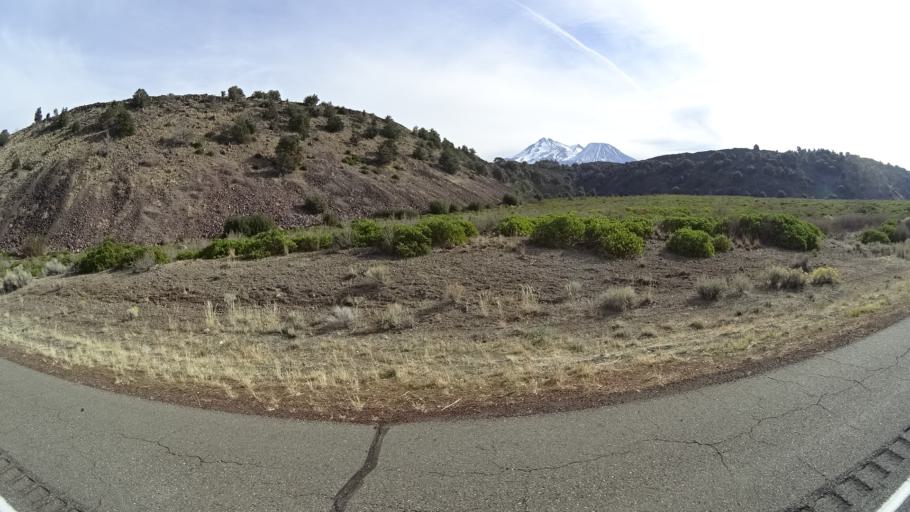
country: US
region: California
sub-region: Siskiyou County
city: Weed
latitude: 41.5188
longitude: -122.3078
